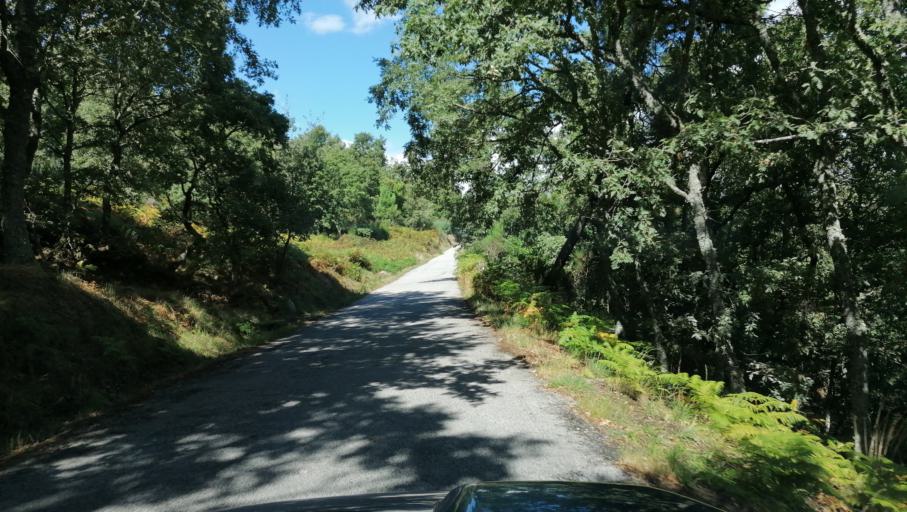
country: PT
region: Vila Real
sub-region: Vila Pouca de Aguiar
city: Vila Pouca de Aguiar
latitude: 41.5574
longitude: -7.6572
